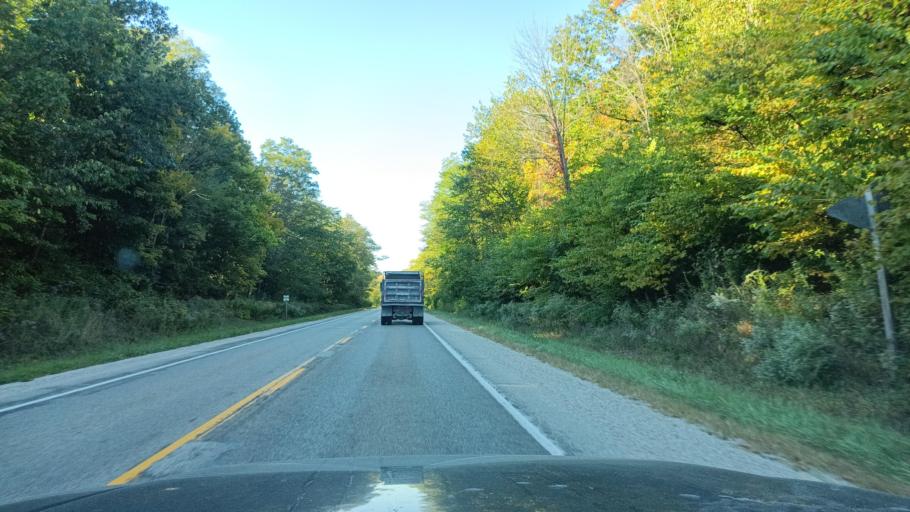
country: US
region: Illinois
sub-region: Clark County
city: Marshall
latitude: 39.4370
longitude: -87.6869
